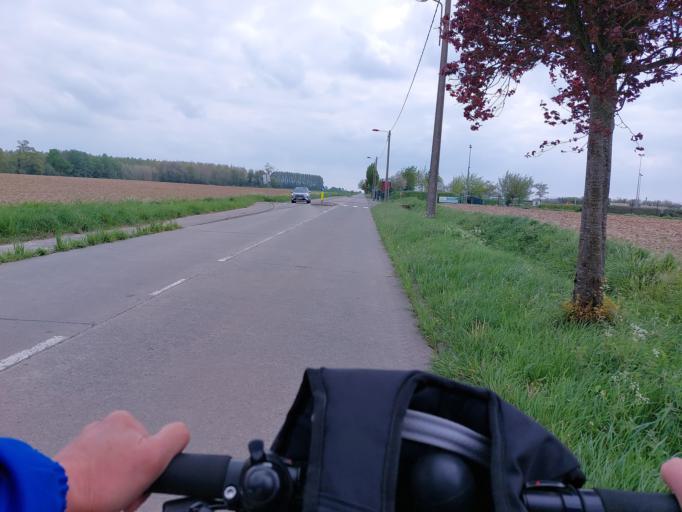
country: BE
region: Wallonia
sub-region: Province du Hainaut
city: Dour
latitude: 50.3608
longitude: 3.7354
